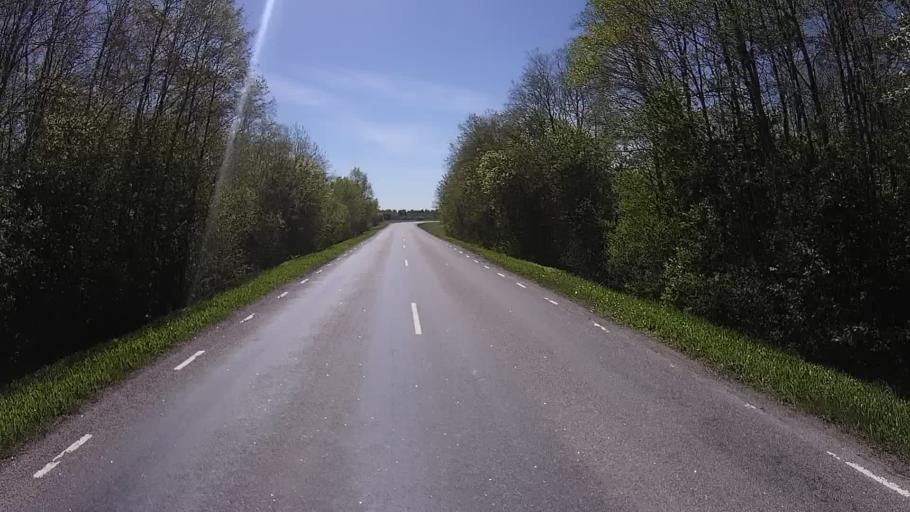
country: EE
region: Harju
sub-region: Rae vald
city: Vaida
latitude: 59.0675
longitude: 25.1554
